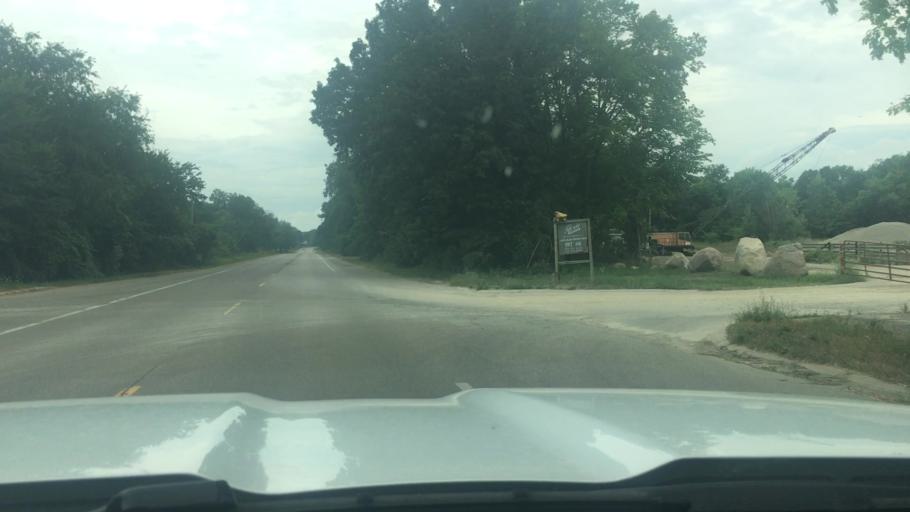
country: US
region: Michigan
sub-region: Kent County
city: Lowell
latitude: 42.9367
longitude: -85.2849
